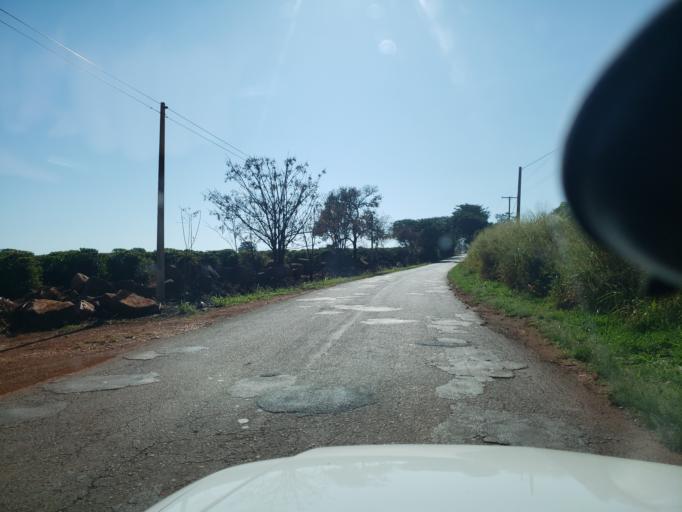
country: BR
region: Sao Paulo
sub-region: Moji-Guacu
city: Mogi-Gaucu
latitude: -22.3437
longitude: -46.8906
